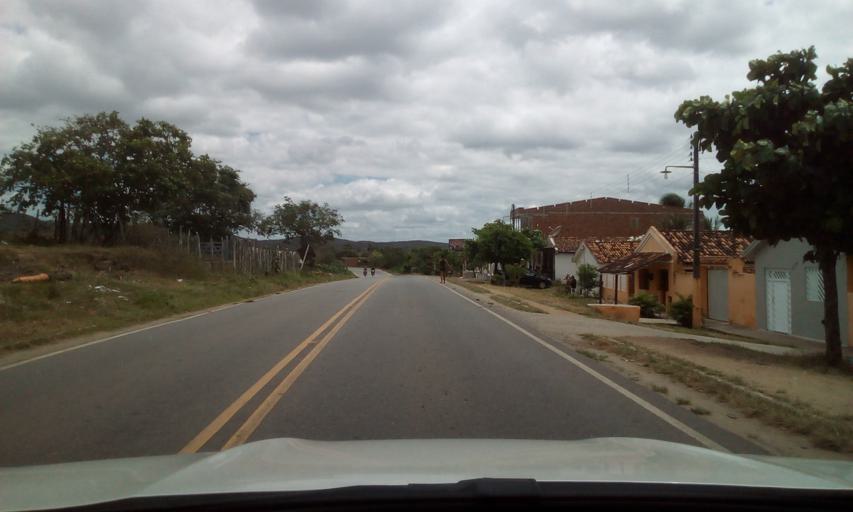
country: BR
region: Paraiba
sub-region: Serra Redonda
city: Alagoa Grande
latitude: -7.1653
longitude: -35.5921
